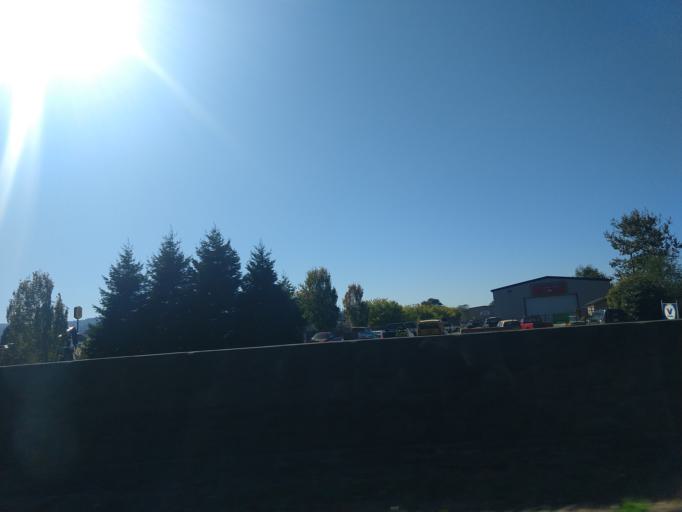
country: US
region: California
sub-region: Humboldt County
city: Fortuna
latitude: 40.5804
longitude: -124.1506
